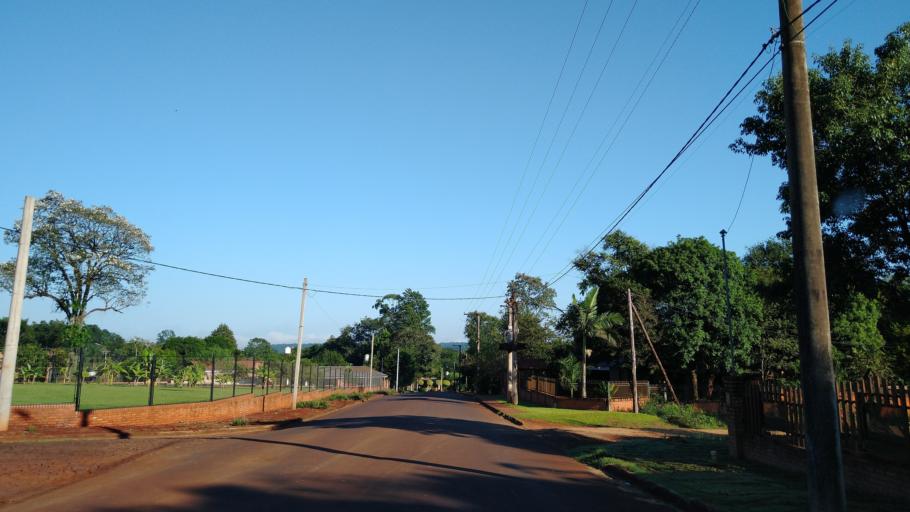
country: AR
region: Misiones
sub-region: Departamento de Montecarlo
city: Montecarlo
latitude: -26.5660
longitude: -54.7503
